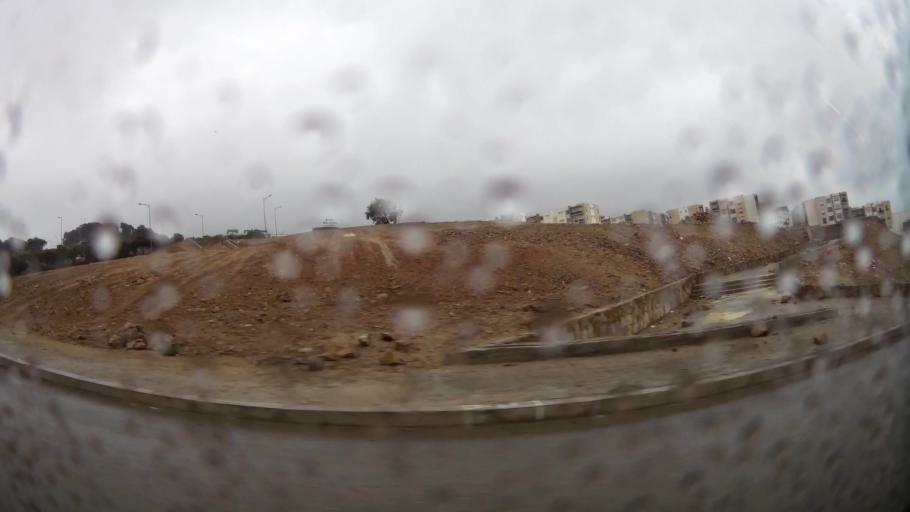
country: MA
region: Taza-Al Hoceima-Taounate
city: Al Hoceima
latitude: 35.2515
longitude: -3.9458
